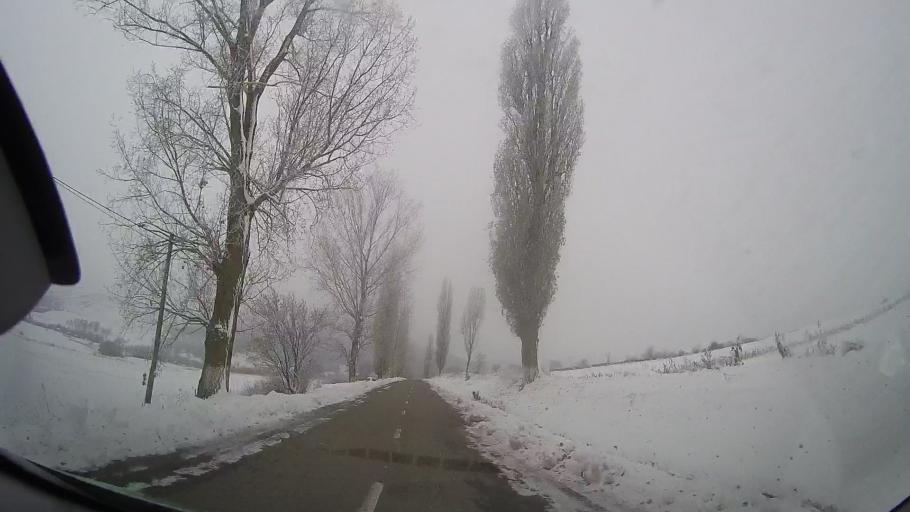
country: RO
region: Neamt
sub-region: Comuna Bozieni
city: Bozieni
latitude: 46.8414
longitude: 27.1682
